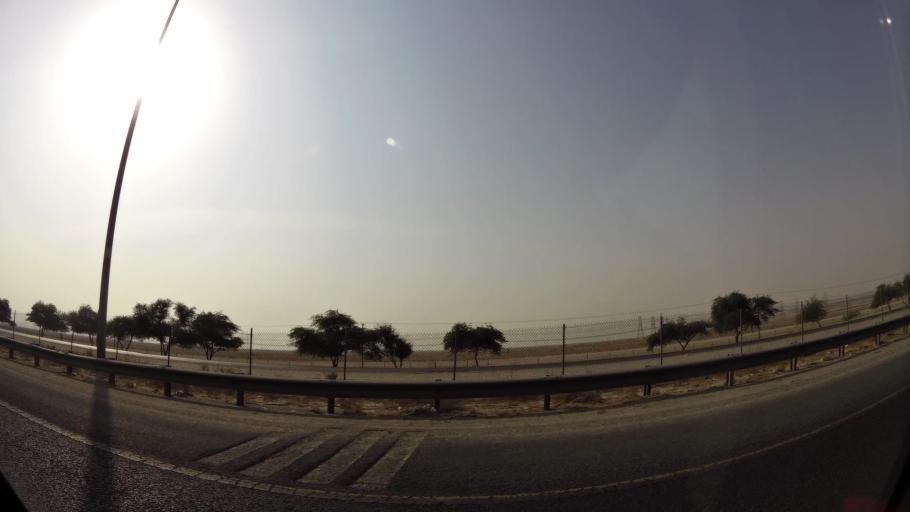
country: KW
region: Al Farwaniyah
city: Janub as Surrah
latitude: 29.1830
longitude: 47.9364
